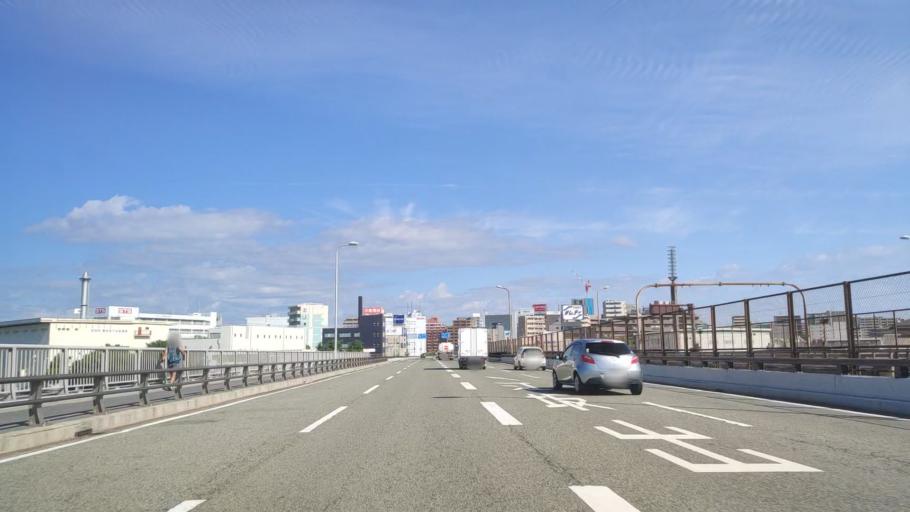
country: JP
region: Osaka
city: Suita
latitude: 34.7489
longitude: 135.4970
